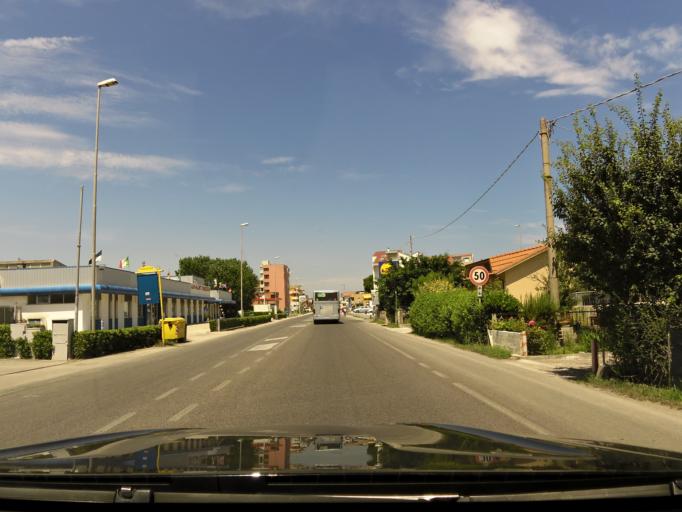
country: IT
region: The Marches
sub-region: Provincia di Pesaro e Urbino
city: Marotta
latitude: 43.7626
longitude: 13.1482
